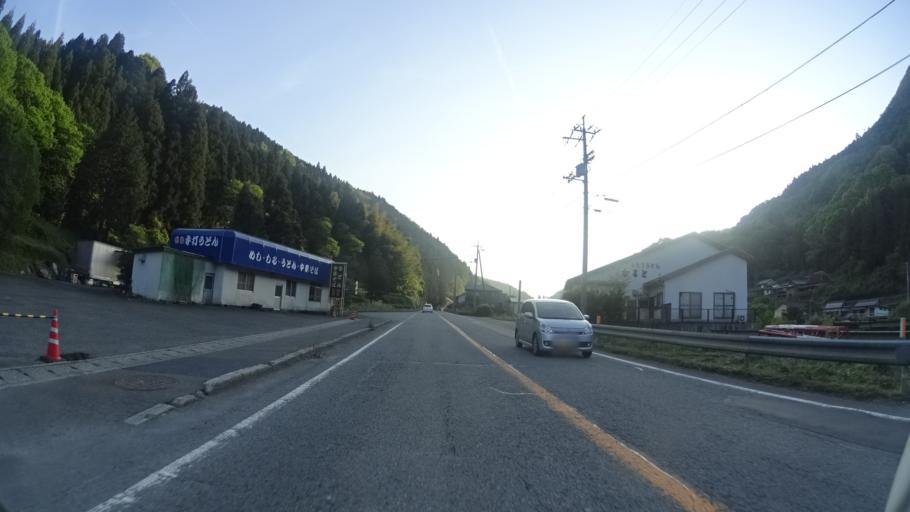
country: JP
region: Tokushima
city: Ikedacho
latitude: 34.0111
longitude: 133.7456
